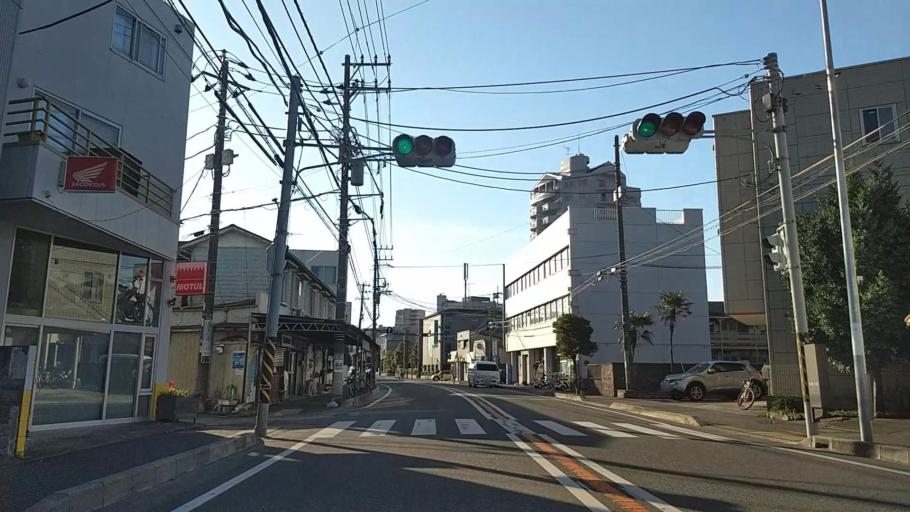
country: JP
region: Kanagawa
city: Fujisawa
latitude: 35.3142
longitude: 139.4860
